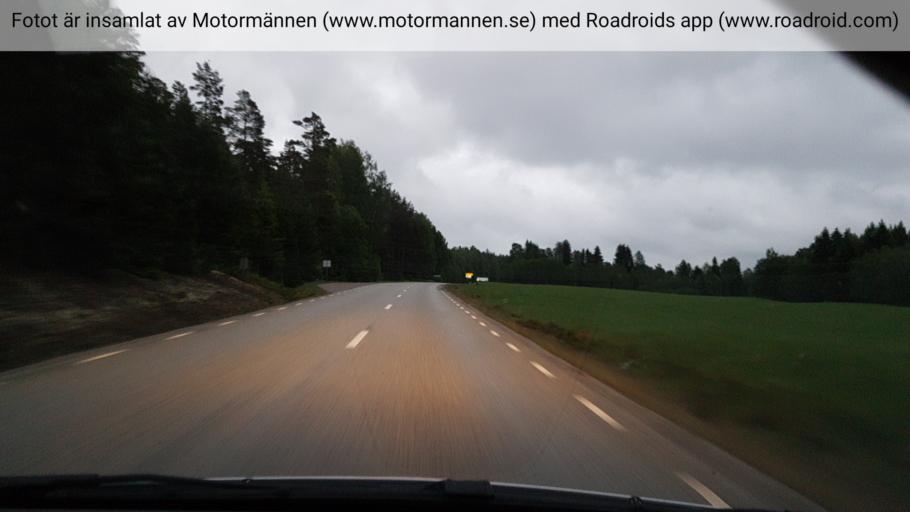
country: SE
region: Vaestmanland
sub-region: Skinnskattebergs Kommun
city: Skinnskatteberg
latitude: 59.9115
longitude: 15.4750
